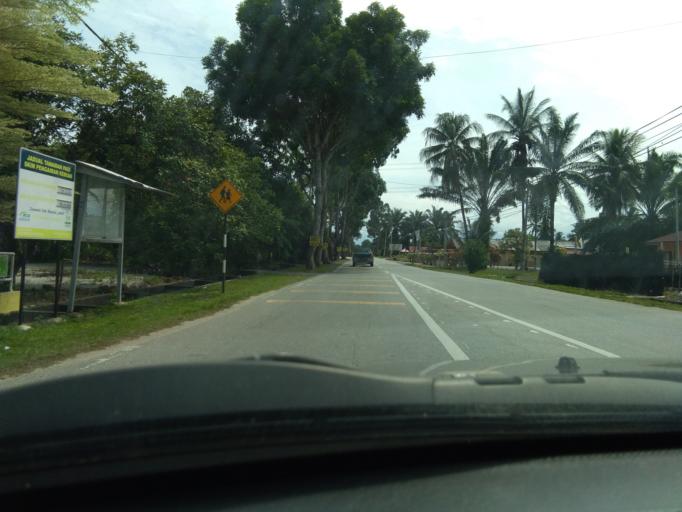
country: MY
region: Perak
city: Bagan Serai
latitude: 5.0523
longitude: 100.5889
